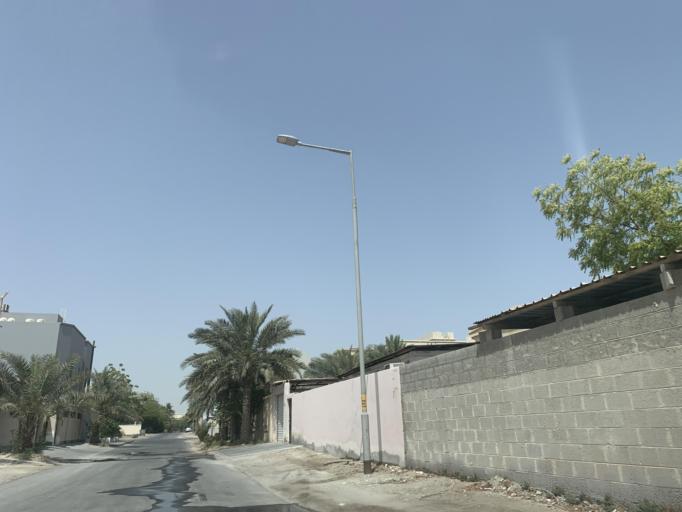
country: BH
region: Northern
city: Sitrah
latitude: 26.1563
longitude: 50.5863
